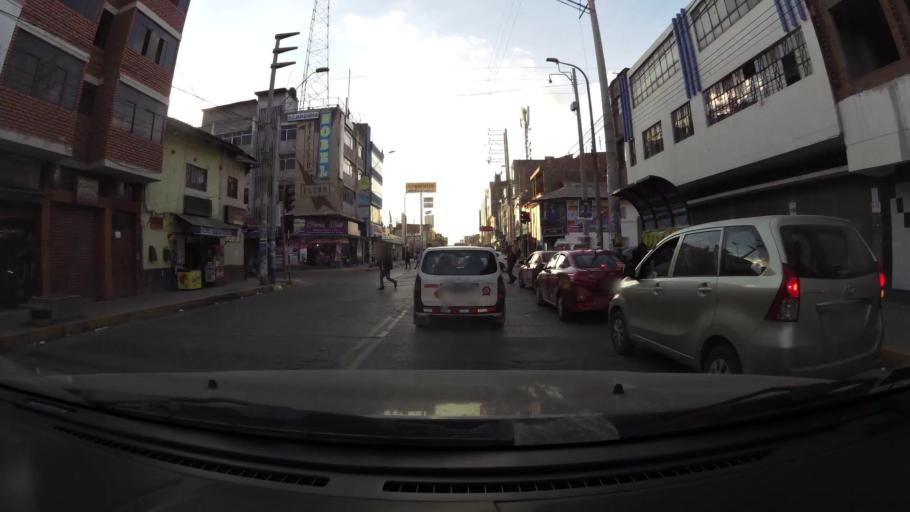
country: PE
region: Junin
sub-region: Provincia de Huancayo
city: El Tambo
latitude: -12.0631
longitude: -75.2136
